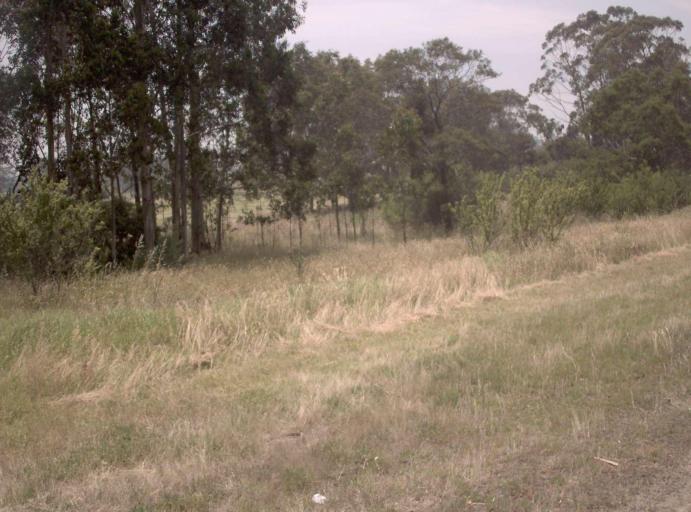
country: AU
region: Victoria
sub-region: Latrobe
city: Traralgon
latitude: -38.2452
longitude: 146.6470
